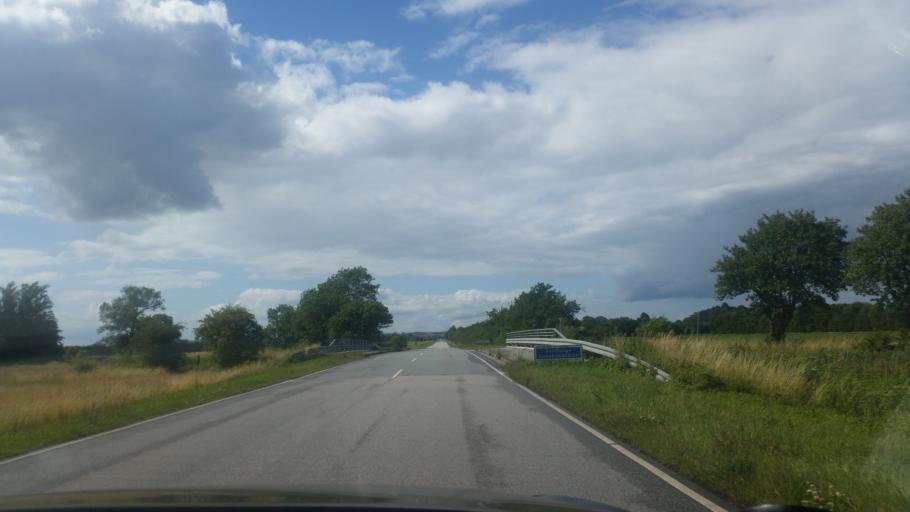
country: DK
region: Zealand
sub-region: Holbaek Kommune
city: Svinninge
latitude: 55.7508
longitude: 11.5236
